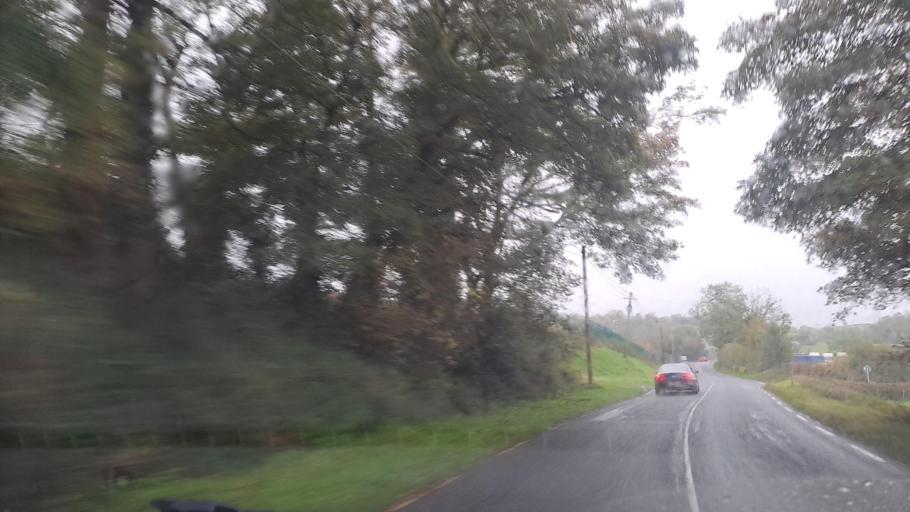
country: IE
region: Ulster
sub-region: County Monaghan
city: Monaghan
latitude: 54.2235
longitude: -6.9347
